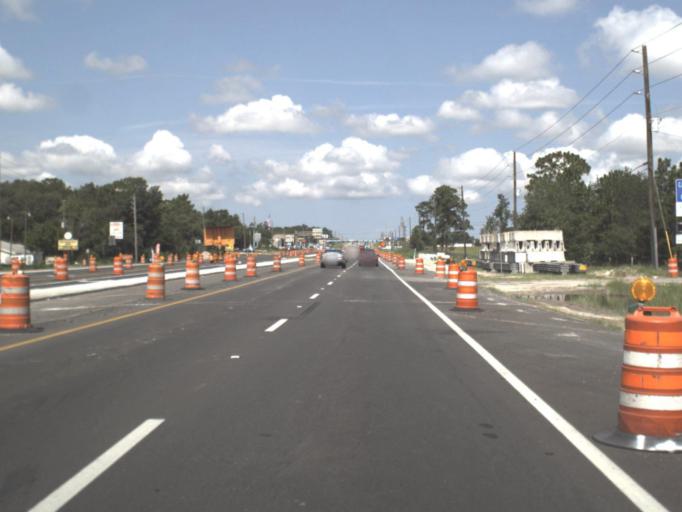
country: US
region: Florida
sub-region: Hernando County
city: Brookridge
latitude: 28.5340
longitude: -82.4838
